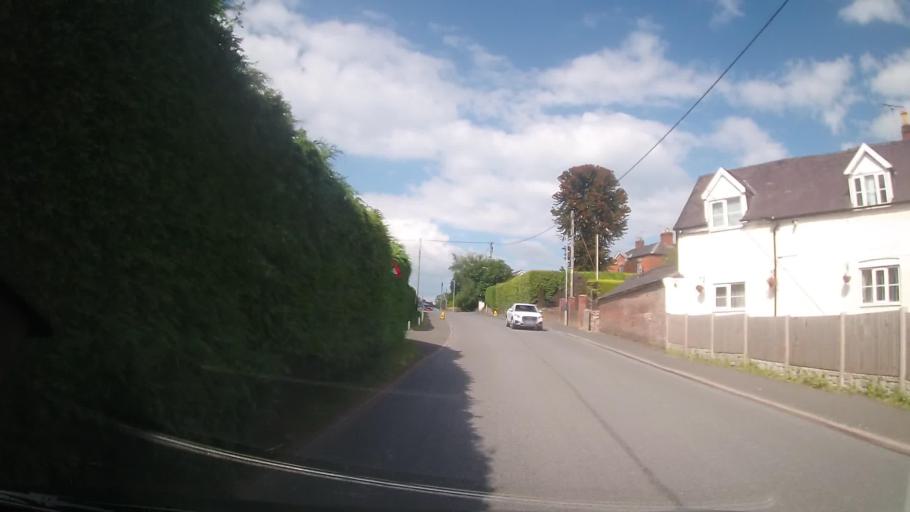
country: GB
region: England
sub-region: Shropshire
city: Whittington
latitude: 52.8757
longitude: -3.0009
